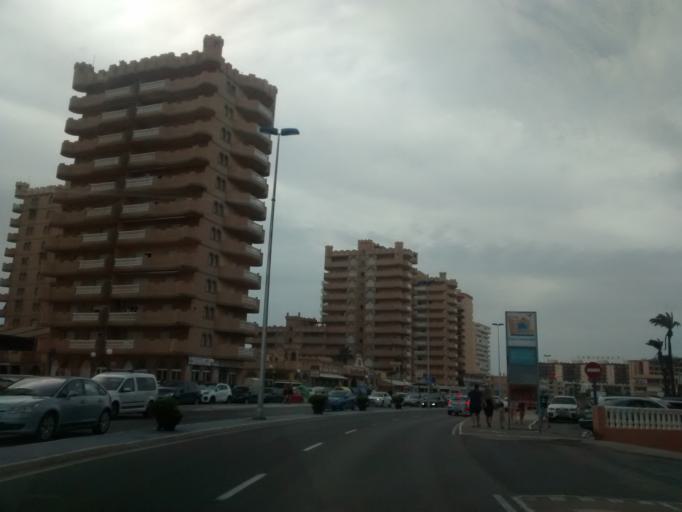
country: ES
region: Murcia
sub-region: Murcia
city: La Manga del Mar Menor
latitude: 37.6775
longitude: -0.7327
